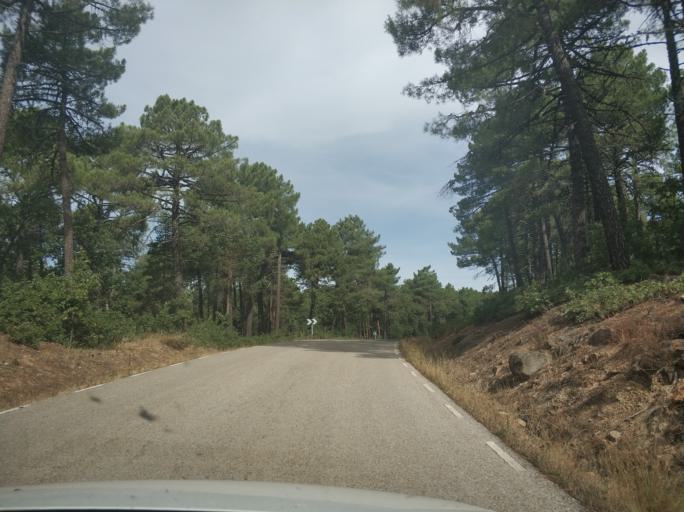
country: ES
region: Castille and Leon
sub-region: Provincia de Soria
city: Duruelo de la Sierra
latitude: 41.8924
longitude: -2.9452
